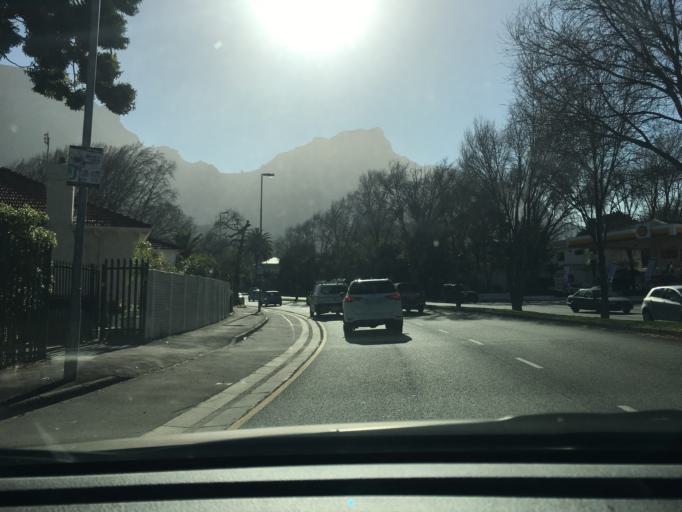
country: ZA
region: Western Cape
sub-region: City of Cape Town
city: Newlands
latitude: -33.9806
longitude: 18.4533
